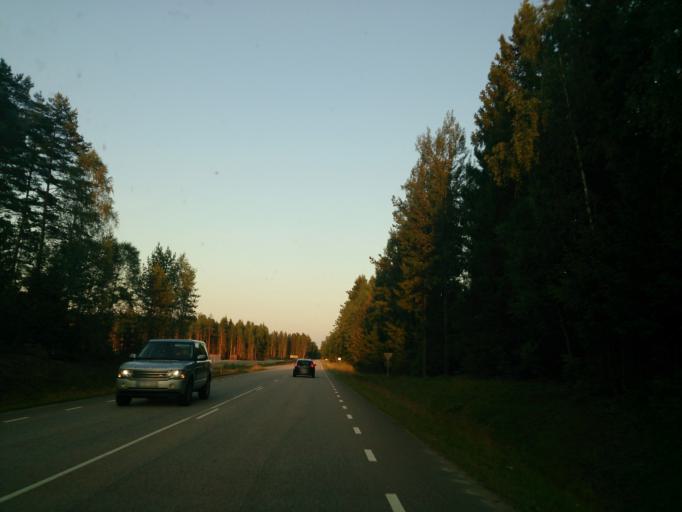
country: SE
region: Kronoberg
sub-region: Alvesta Kommun
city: Alvesta
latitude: 56.9137
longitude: 14.5019
